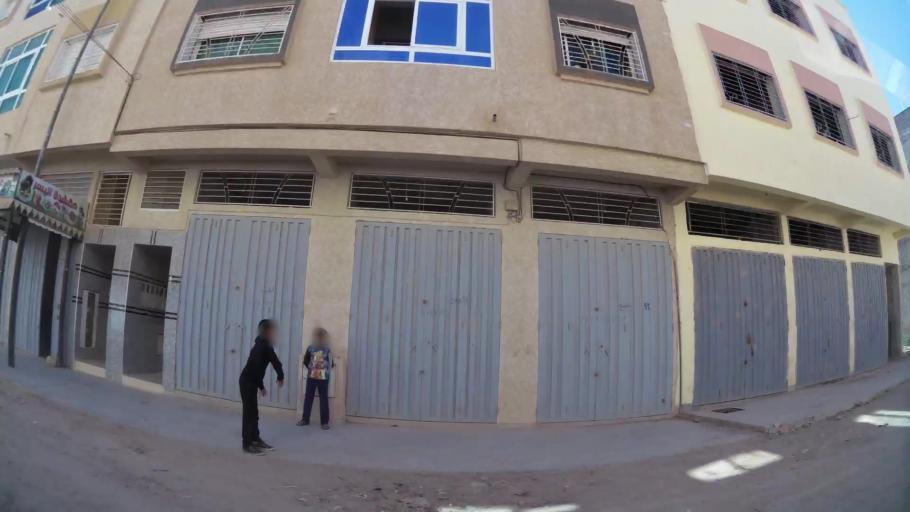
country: MA
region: Fes-Boulemane
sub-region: Fes
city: Fes
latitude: 33.9982
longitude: -5.0079
